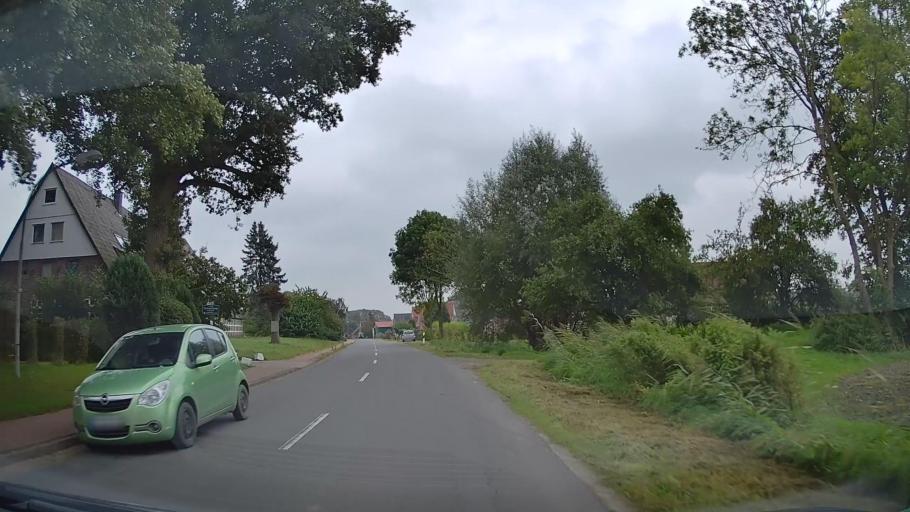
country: DE
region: Lower Saxony
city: Geversdorf
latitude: 53.8214
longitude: 9.0830
